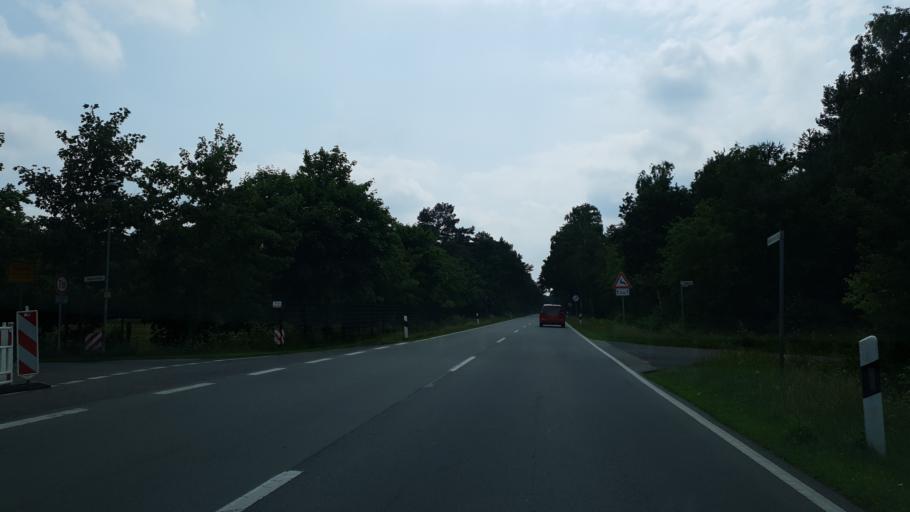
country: DE
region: Lower Saxony
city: Geeste
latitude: 52.5629
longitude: 7.2029
